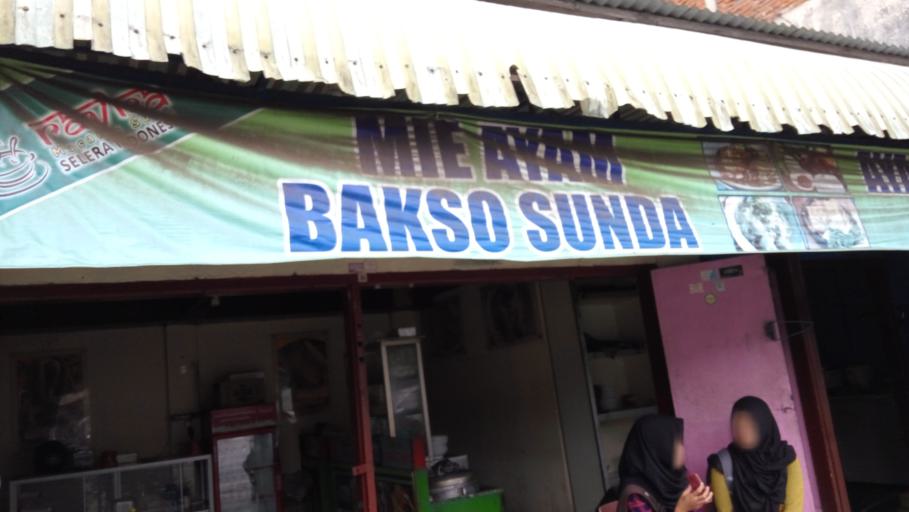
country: ID
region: East Java
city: Malang
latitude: -7.9649
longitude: 112.6139
